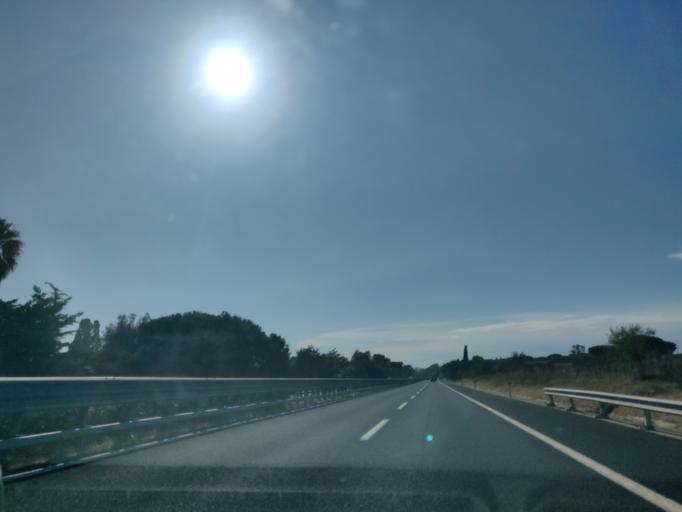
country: IT
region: Latium
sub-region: Citta metropolitana di Roma Capitale
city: Valcanneto
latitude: 41.9355
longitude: 12.1601
